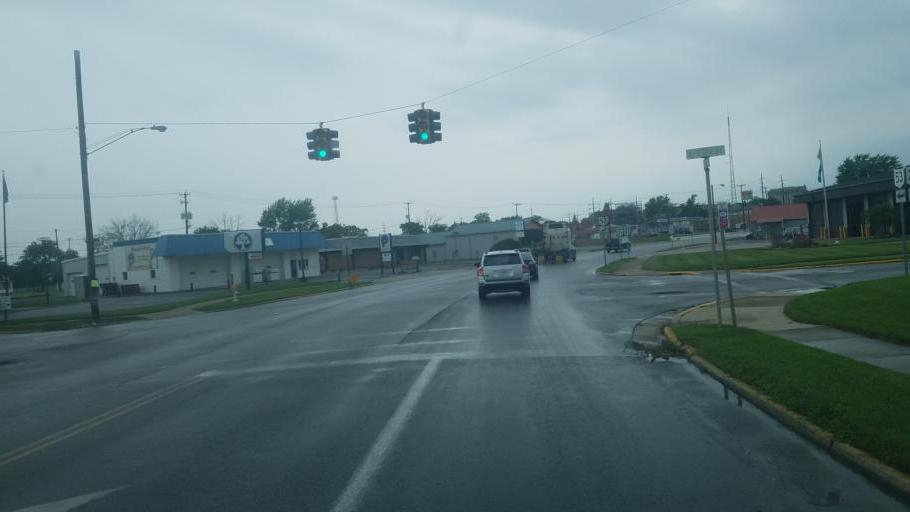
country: US
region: Ohio
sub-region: Hardin County
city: Kenton
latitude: 40.6415
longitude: -83.6078
